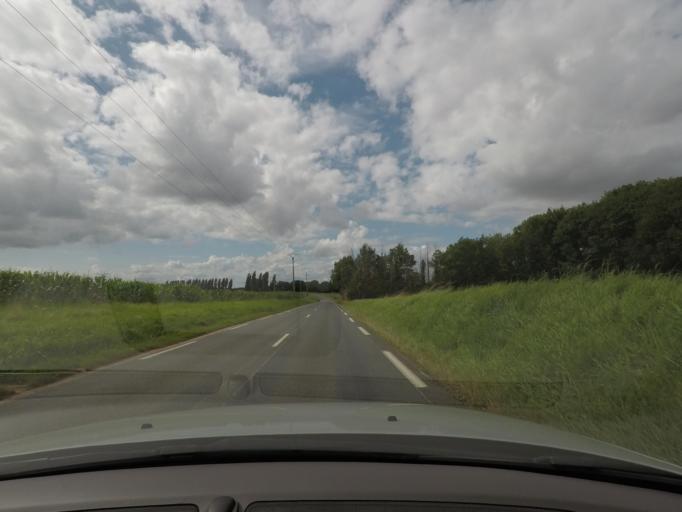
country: FR
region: Haute-Normandie
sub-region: Departement de l'Eure
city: Les Andelys
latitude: 49.2349
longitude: 1.4296
